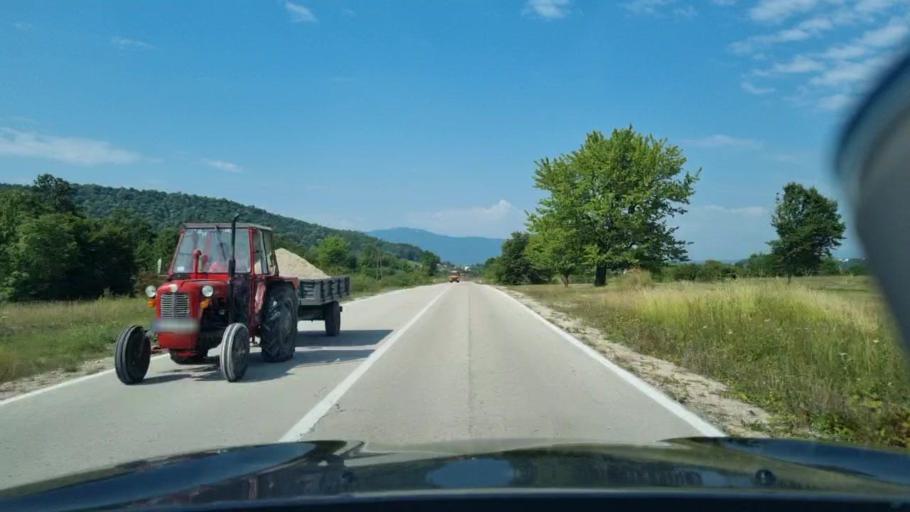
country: BA
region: Federation of Bosnia and Herzegovina
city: Ostrozac
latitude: 44.8841
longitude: 15.9240
